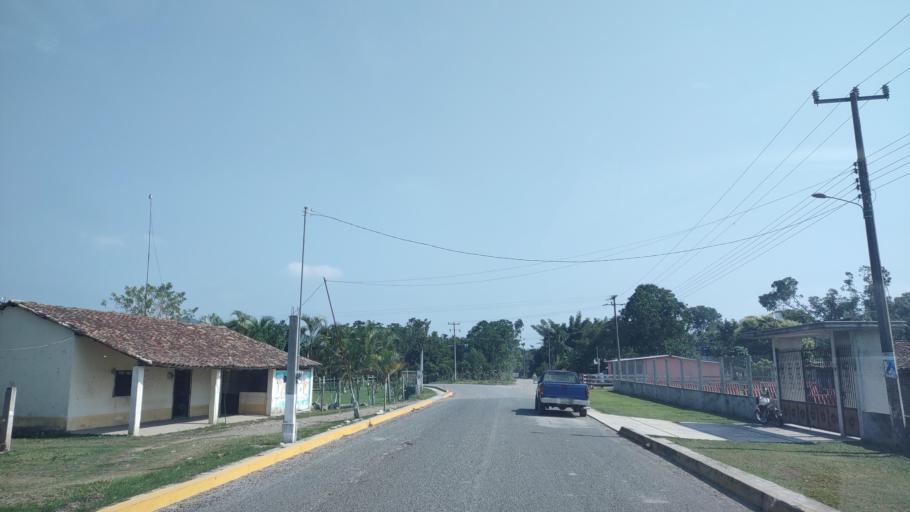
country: MX
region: Veracruz
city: Agua Dulce
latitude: 20.2636
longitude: -97.3077
